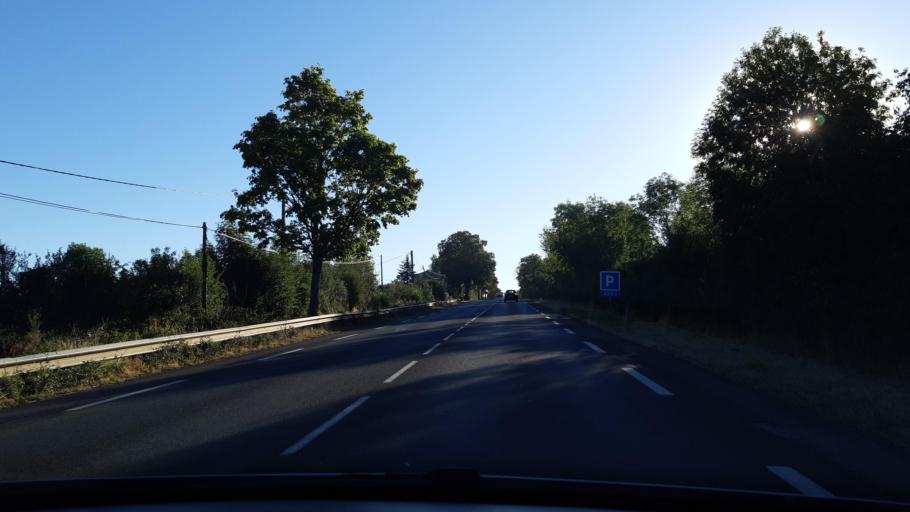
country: FR
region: Poitou-Charentes
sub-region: Departement des Deux-Sevres
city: Azay-le-Brule
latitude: 46.3948
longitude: -0.2507
